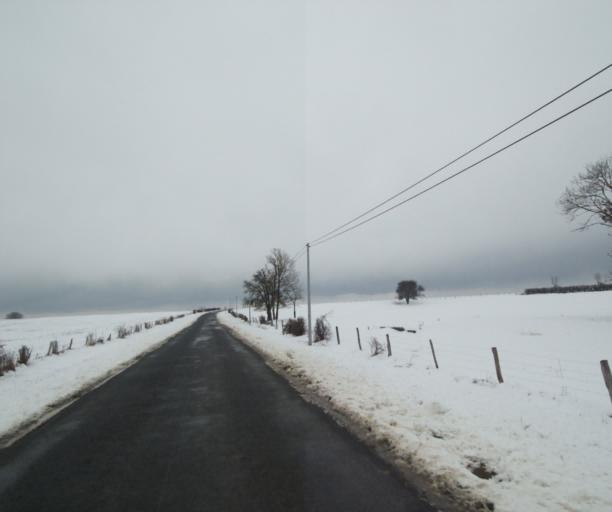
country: FR
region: Champagne-Ardenne
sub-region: Departement de la Haute-Marne
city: Laneuville-a-Remy
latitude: 48.4961
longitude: 4.8679
